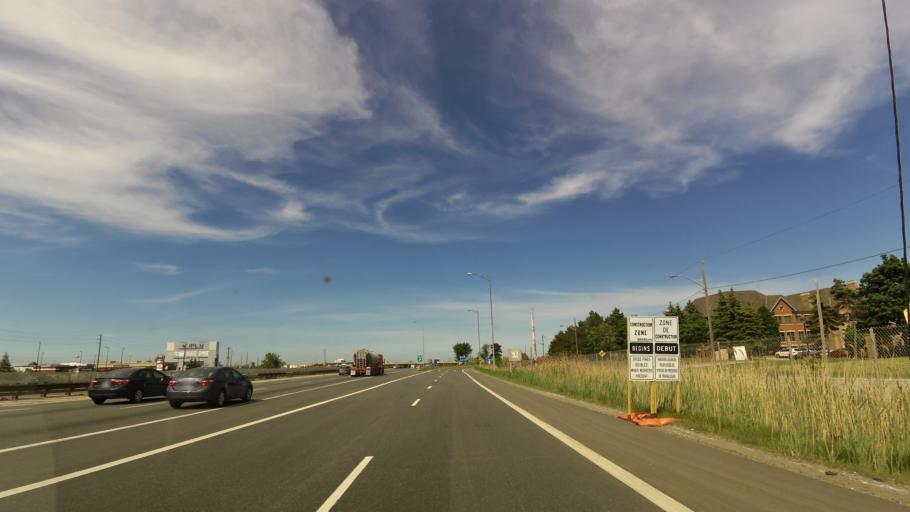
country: CA
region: Ontario
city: Oakville
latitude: 43.5063
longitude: -79.6668
